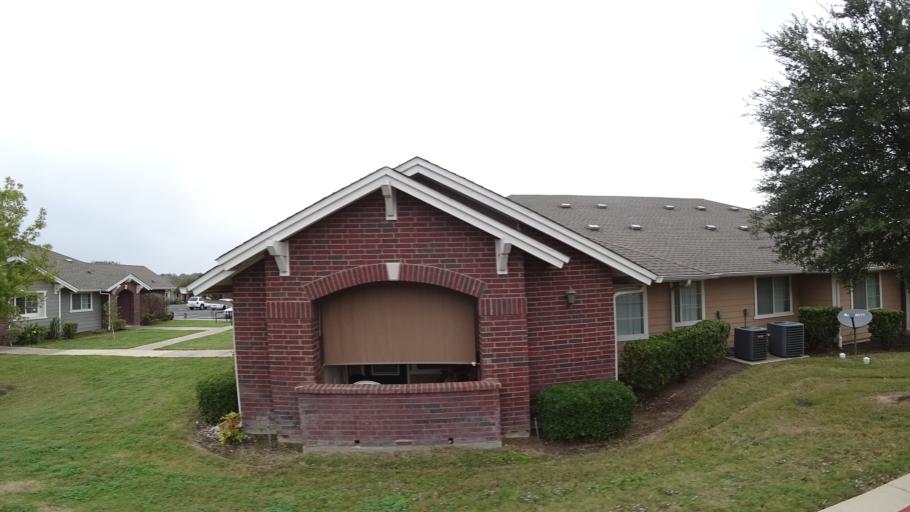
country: US
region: Texas
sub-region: Travis County
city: Pflugerville
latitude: 30.4306
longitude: -97.6198
